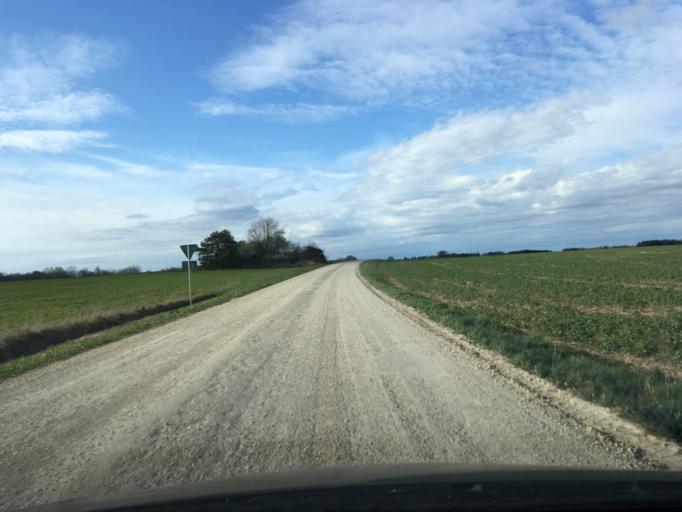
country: EE
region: Raplamaa
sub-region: Maerjamaa vald
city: Marjamaa
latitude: 58.9287
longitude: 24.3068
